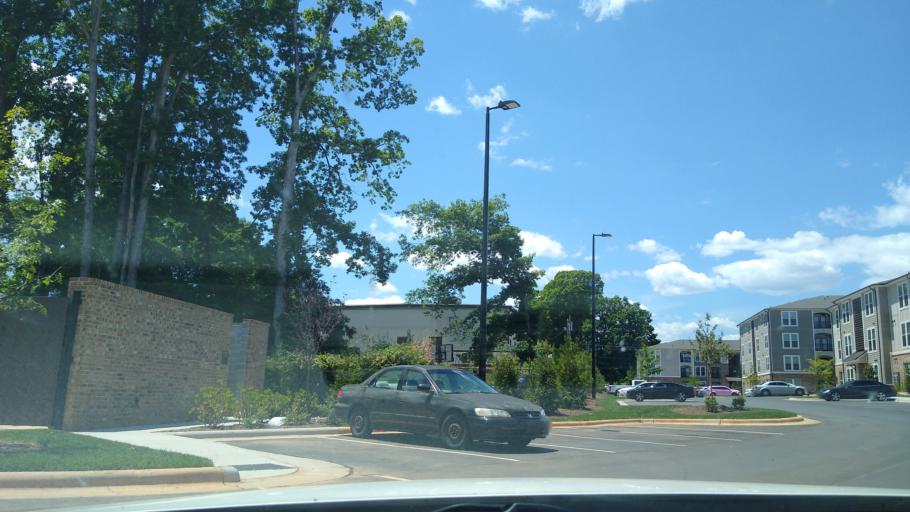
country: US
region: North Carolina
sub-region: Guilford County
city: Jamestown
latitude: 36.0661
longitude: -79.9074
